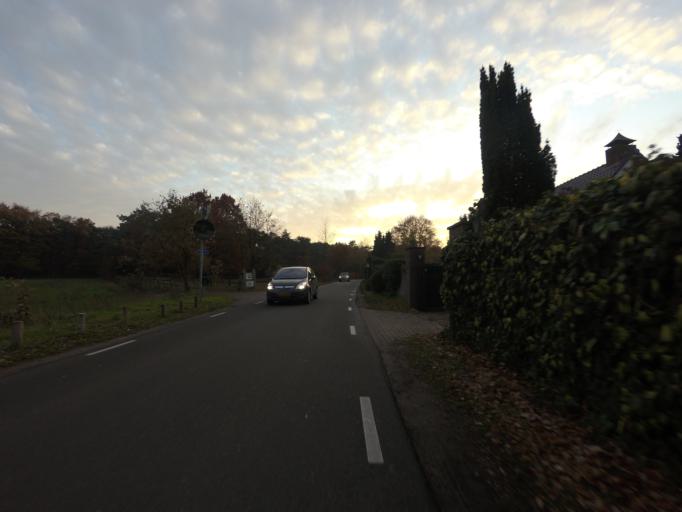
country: NL
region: North Brabant
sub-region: Gemeente Breda
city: Breda
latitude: 51.5206
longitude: 4.7615
